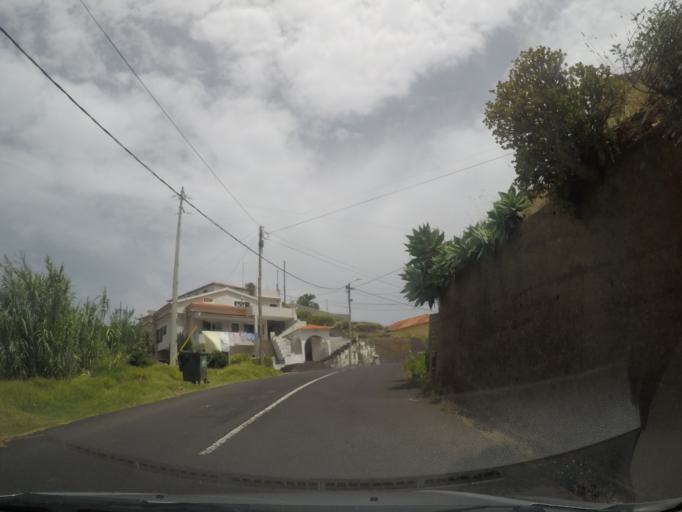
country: PT
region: Madeira
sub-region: Santa Cruz
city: Camacha
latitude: 32.6707
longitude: -16.8400
